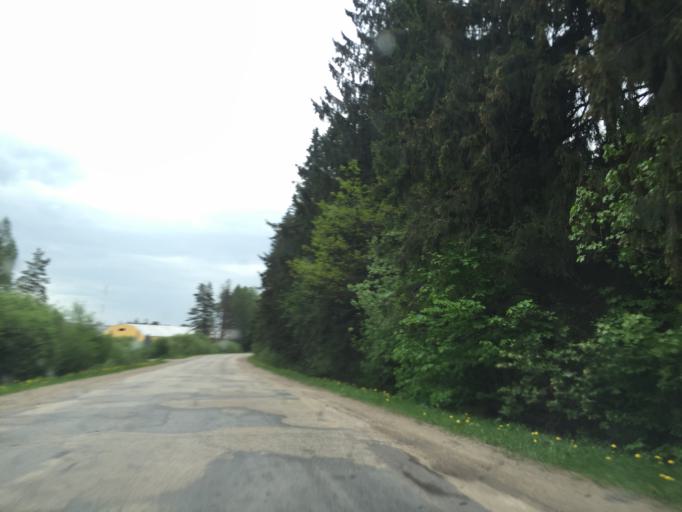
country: LV
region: Ogre
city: Ogre
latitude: 56.8276
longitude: 24.5957
